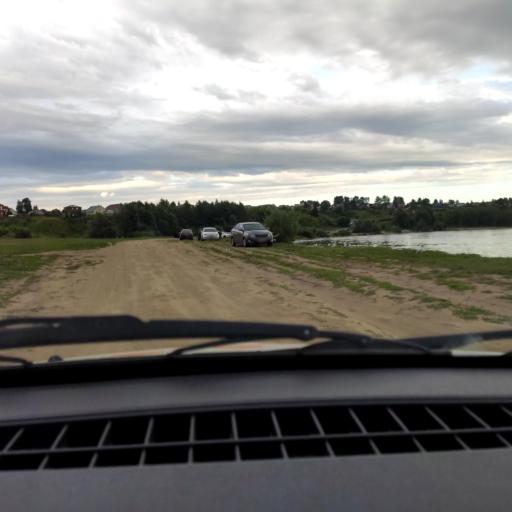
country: RU
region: Bashkortostan
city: Iglino
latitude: 54.7979
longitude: 56.2292
